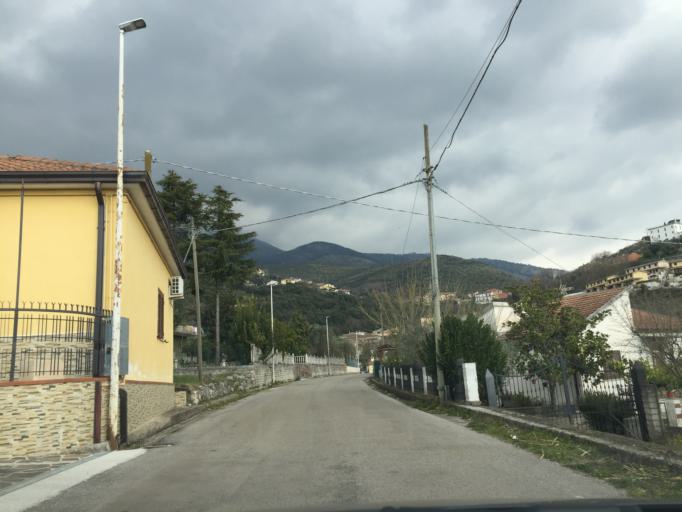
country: IT
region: Latium
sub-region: Provincia di Frosinone
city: Piedimonte San Germano Alta
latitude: 41.5027
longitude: 13.7452
